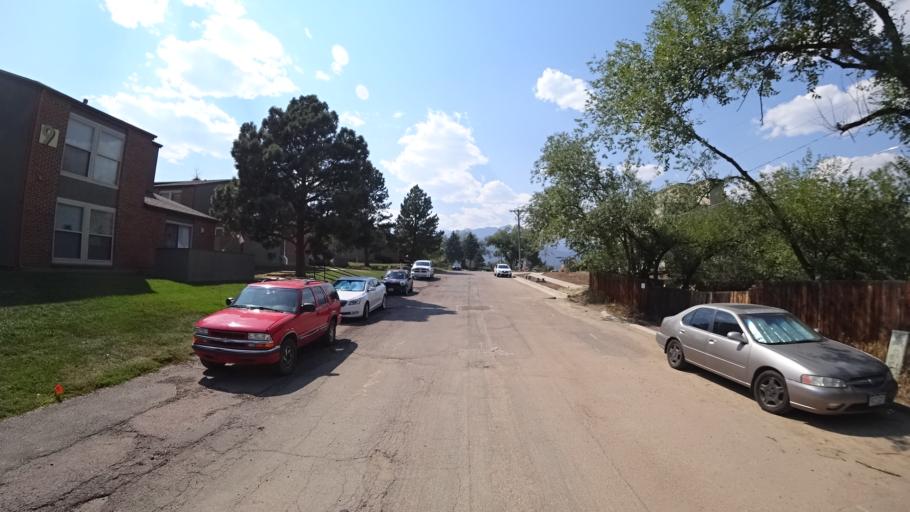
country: US
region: Colorado
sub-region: El Paso County
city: Colorado Springs
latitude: 38.8030
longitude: -104.8271
